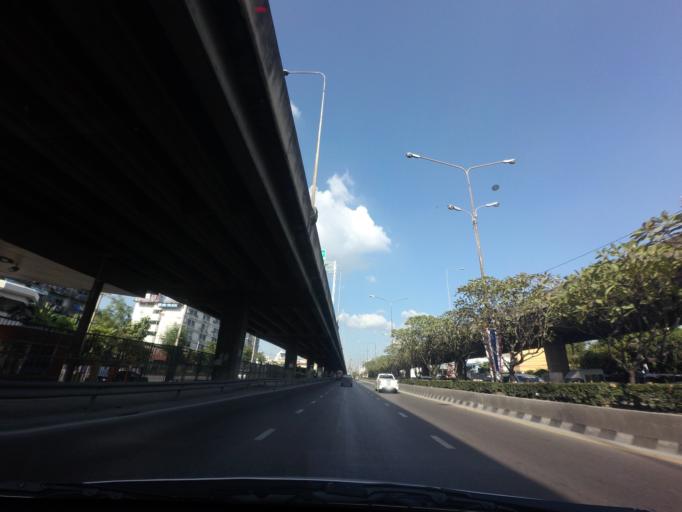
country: TH
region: Bangkok
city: Yan Nawa
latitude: 13.7078
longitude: 100.5485
